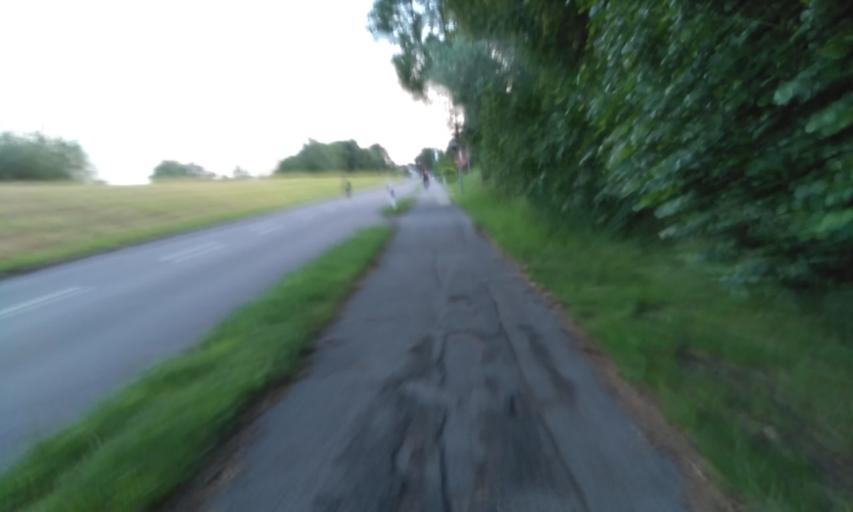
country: DE
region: Lower Saxony
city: Buxtehude
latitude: 53.4863
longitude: 9.7062
